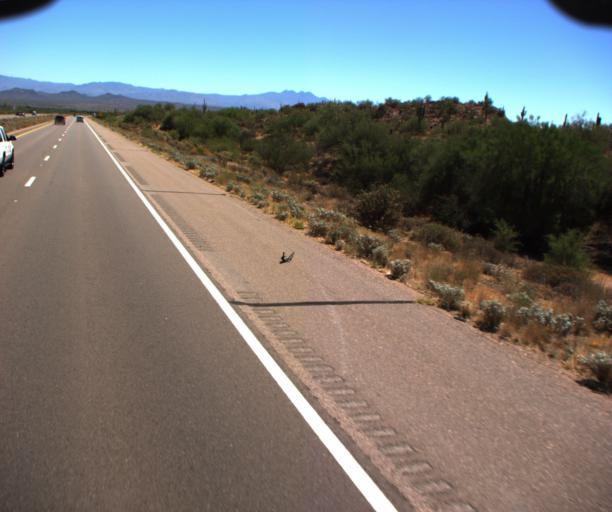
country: US
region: Arizona
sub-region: Maricopa County
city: Fountain Hills
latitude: 33.5699
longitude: -111.7010
